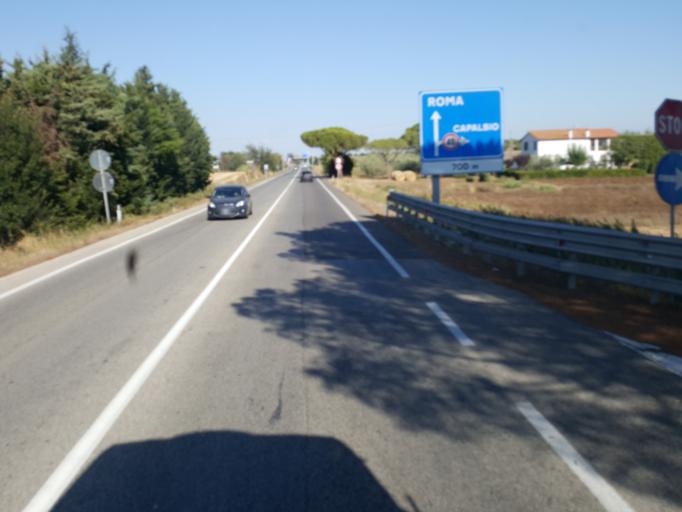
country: IT
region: Tuscany
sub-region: Provincia di Grosseto
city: Capalbio
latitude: 42.4148
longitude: 11.4014
